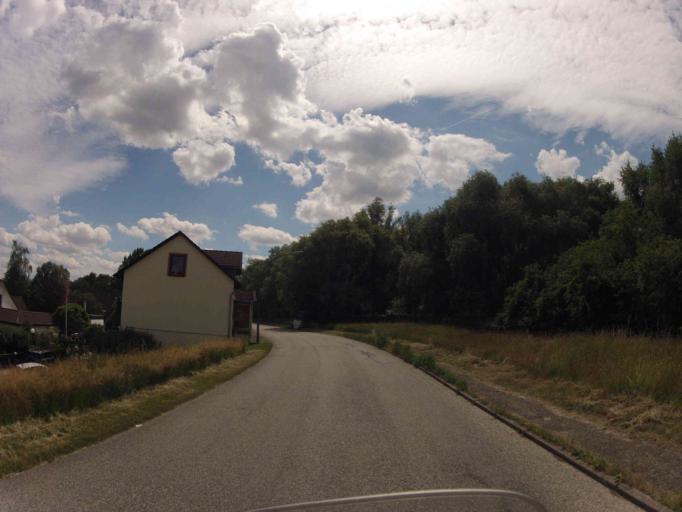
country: DE
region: Hamburg
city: Rothenburgsort
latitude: 53.5100
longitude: 10.0749
